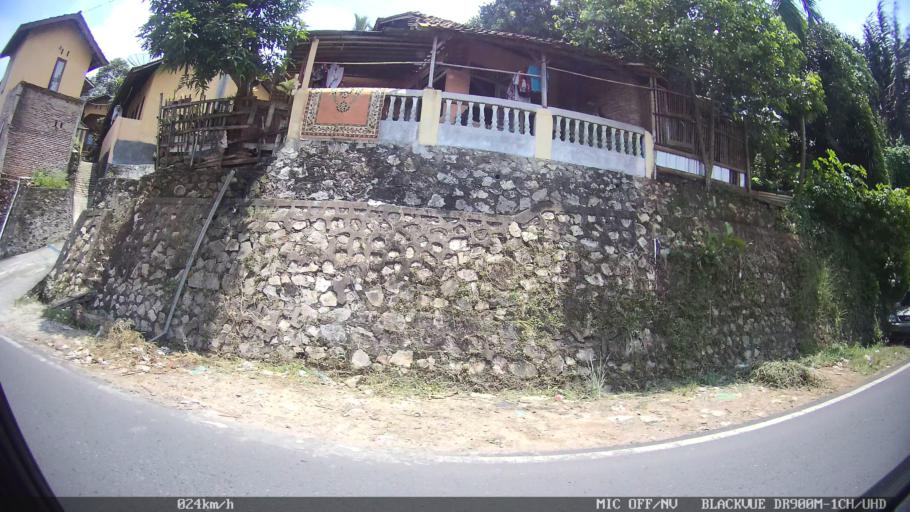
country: ID
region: Lampung
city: Kedaton
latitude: -5.3991
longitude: 105.2534
